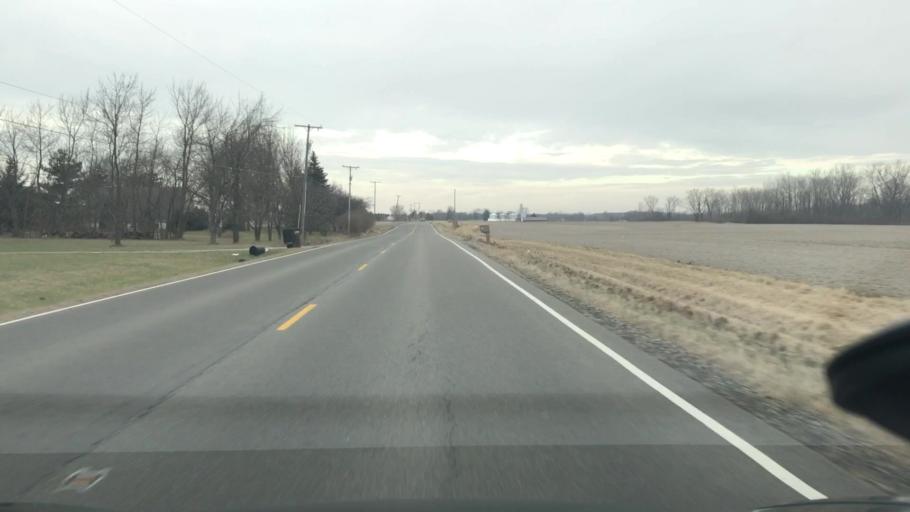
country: US
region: Ohio
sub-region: Madison County
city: London
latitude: 39.8391
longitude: -83.3822
